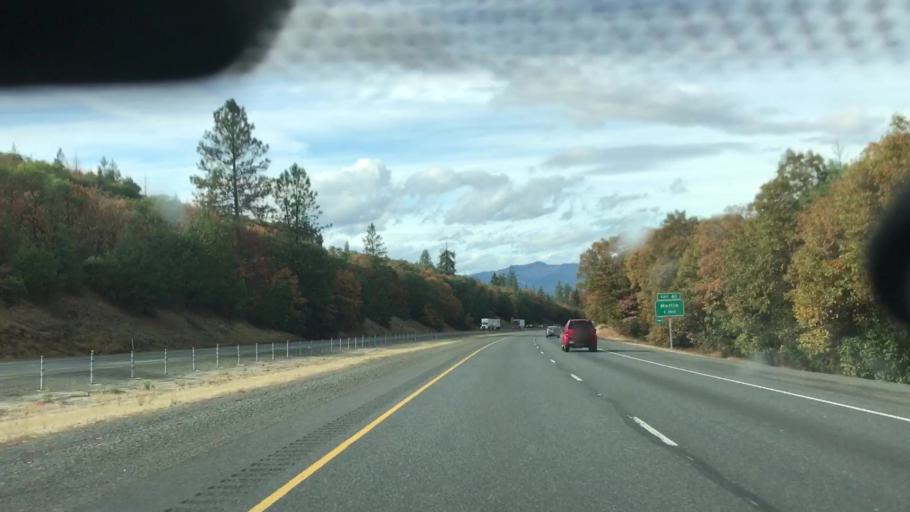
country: US
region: Oregon
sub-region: Josephine County
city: Grants Pass
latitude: 42.4800
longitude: -123.3552
